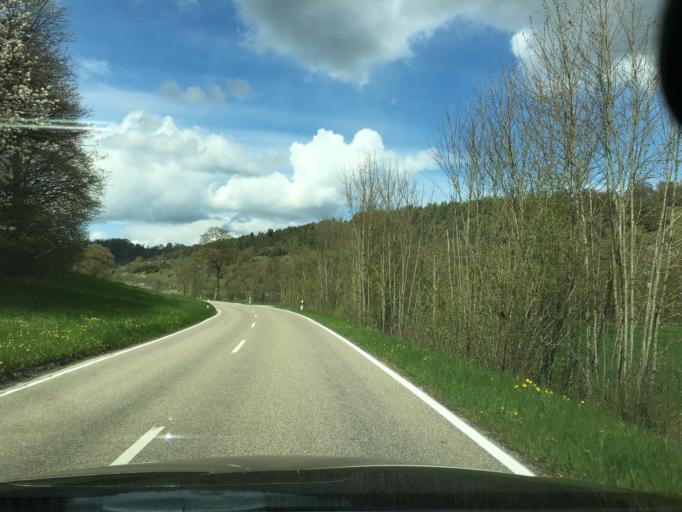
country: DE
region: Bavaria
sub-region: Upper Bavaria
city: Schernfeld
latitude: 48.8781
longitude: 11.0599
